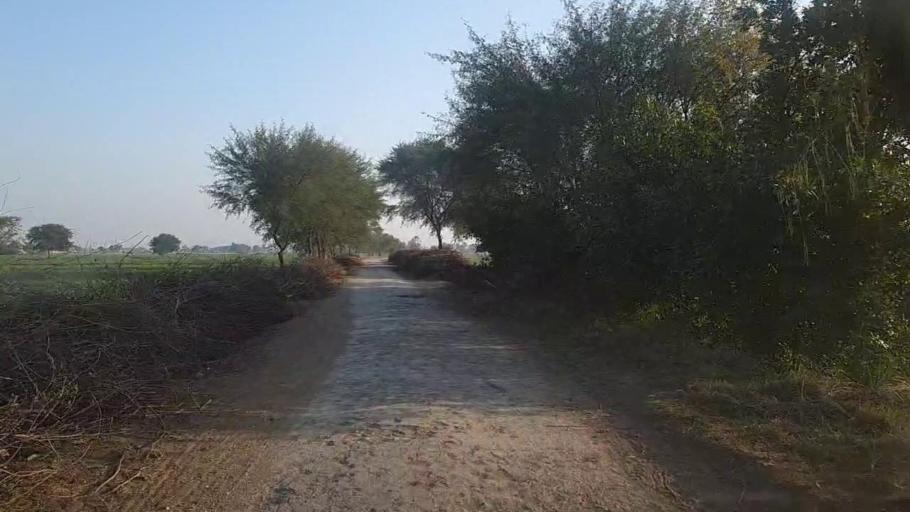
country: PK
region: Sindh
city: Khairpur
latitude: 28.0740
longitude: 69.7487
